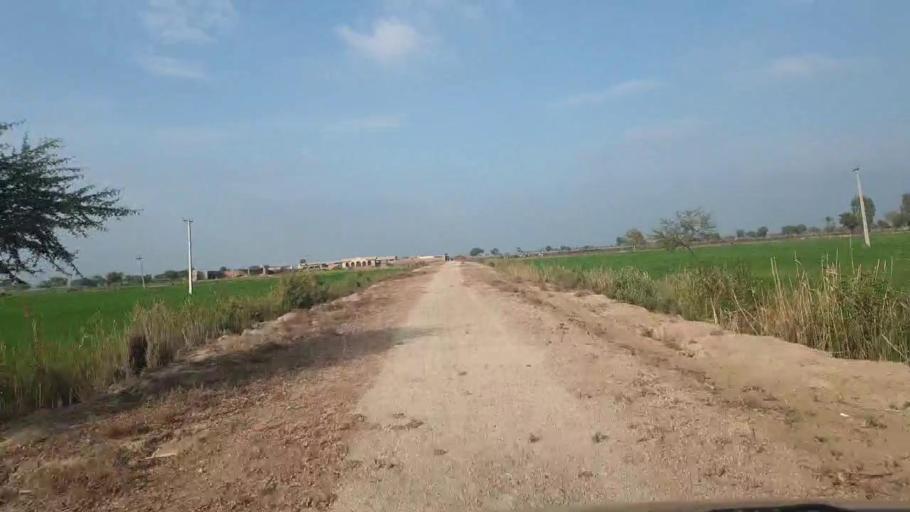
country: PK
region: Sindh
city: Shahdadpur
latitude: 25.8966
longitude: 68.6707
